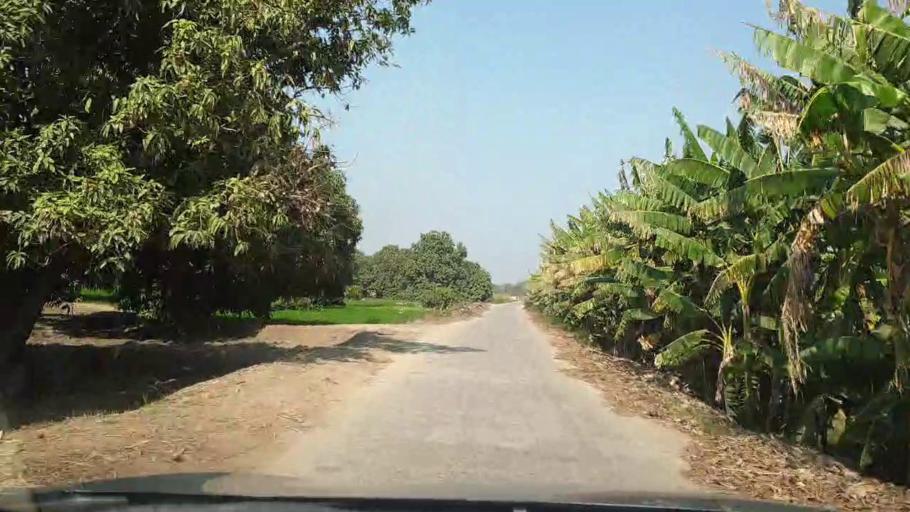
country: PK
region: Sindh
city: Tando Allahyar
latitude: 25.4850
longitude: 68.7915
